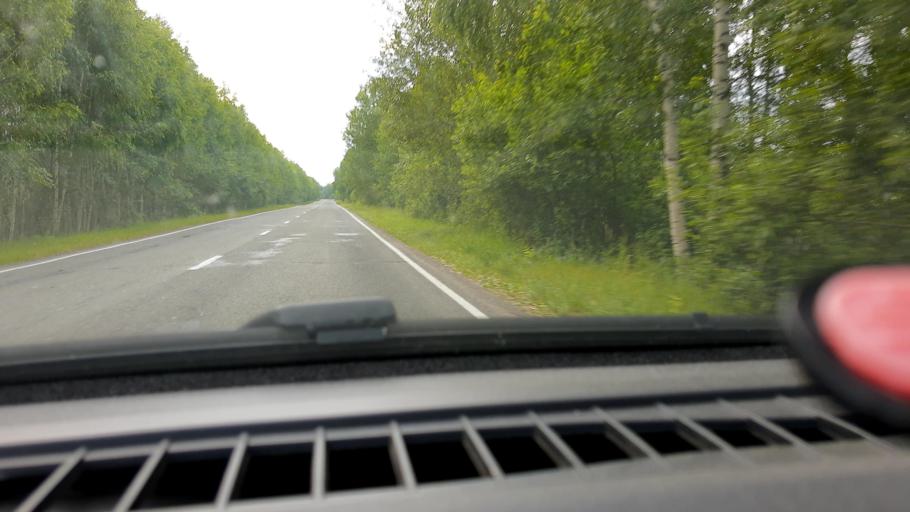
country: RU
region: Nizjnij Novgorod
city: Neklyudovo
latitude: 56.5142
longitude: 43.9376
